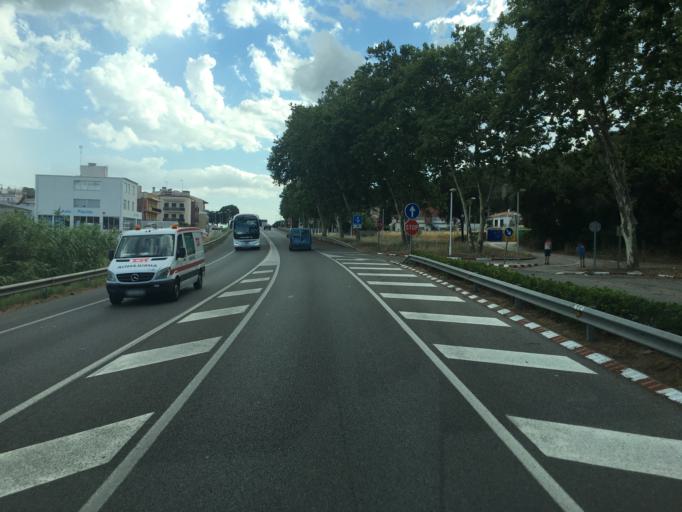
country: ES
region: Catalonia
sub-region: Provincia de Barcelona
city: Malgrat de Mar
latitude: 41.6466
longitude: 2.7313
